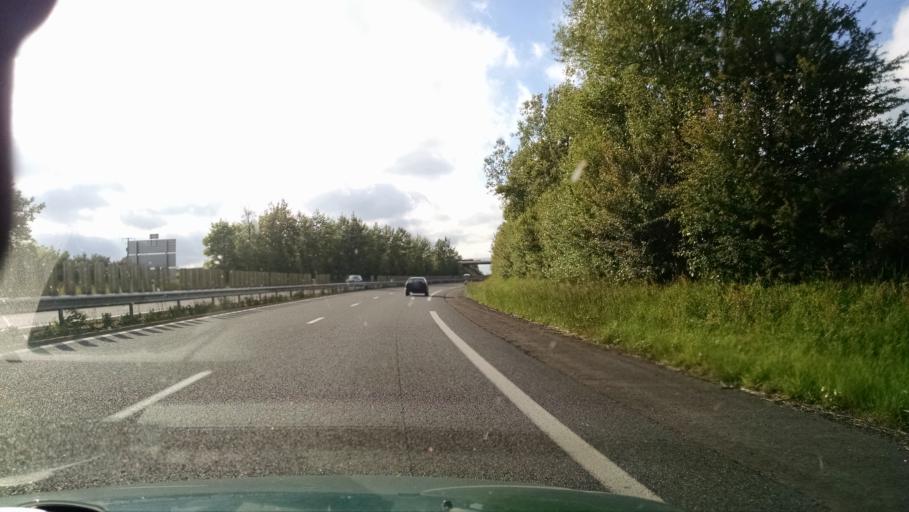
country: FR
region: Brittany
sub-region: Departement du Finistere
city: Henvic
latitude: 48.6297
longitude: -3.9183
